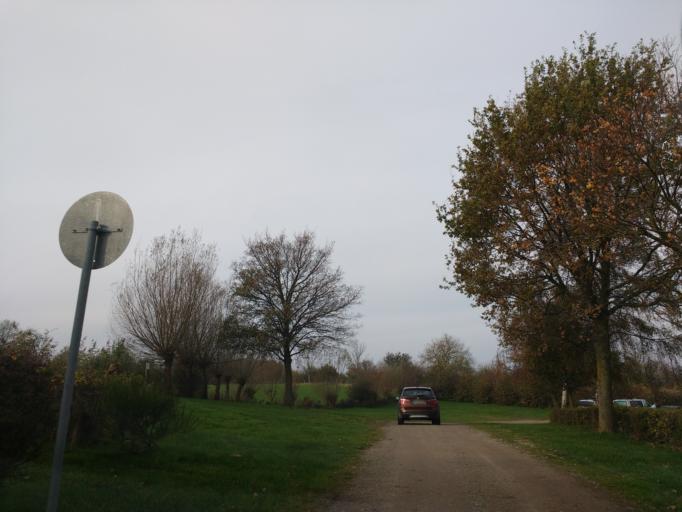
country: DE
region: Mecklenburg-Vorpommern
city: Klutz
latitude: 54.0086
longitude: 11.1466
